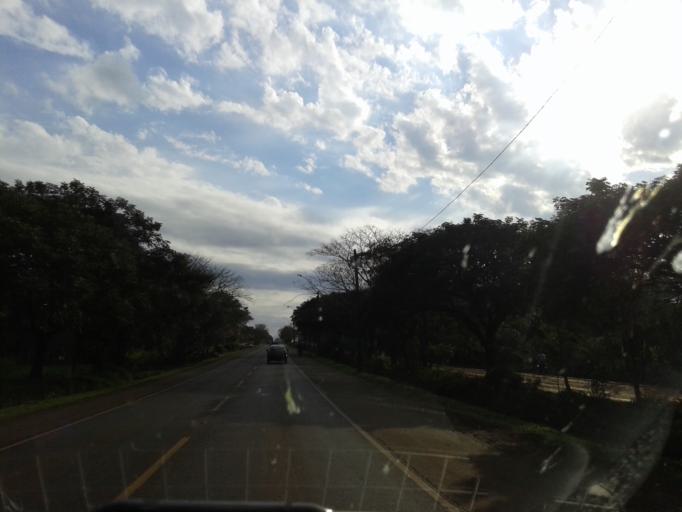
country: PY
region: Itapua
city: Obligado
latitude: -27.0728
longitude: -55.6264
